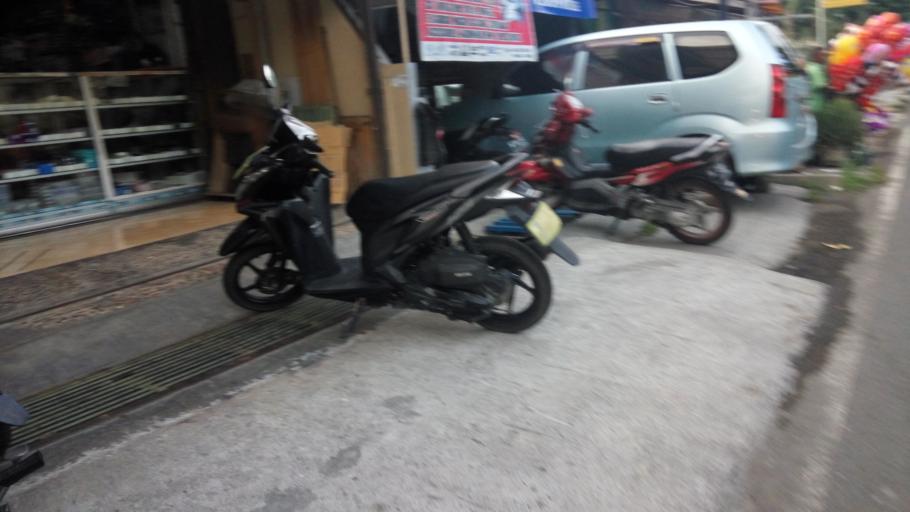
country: ID
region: Central Java
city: Semarang
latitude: -6.9879
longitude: 110.4046
